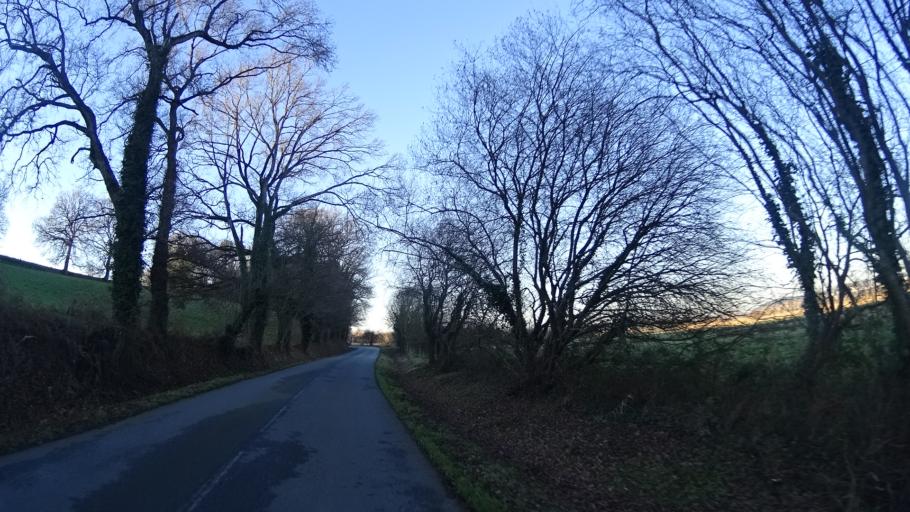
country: FR
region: Brittany
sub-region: Departement du Morbihan
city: Saint-Jean-la-Poterie
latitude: 47.6424
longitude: -2.1154
